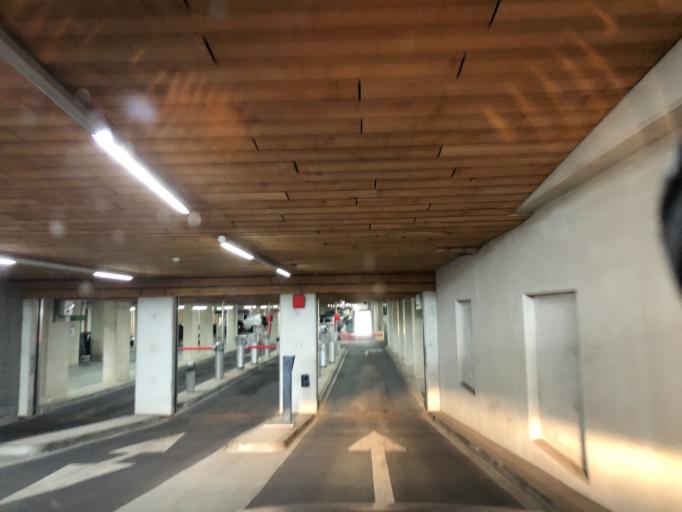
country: NL
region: Groningen
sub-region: Gemeente Groningen
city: Groningen
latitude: 53.2179
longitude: 6.5768
